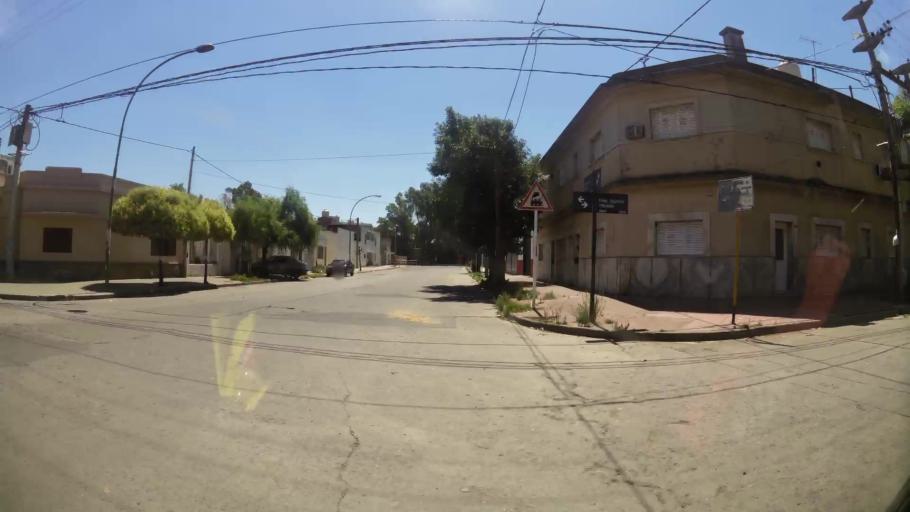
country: AR
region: Cordoba
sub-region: Departamento de Capital
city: Cordoba
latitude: -31.3924
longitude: -64.1918
